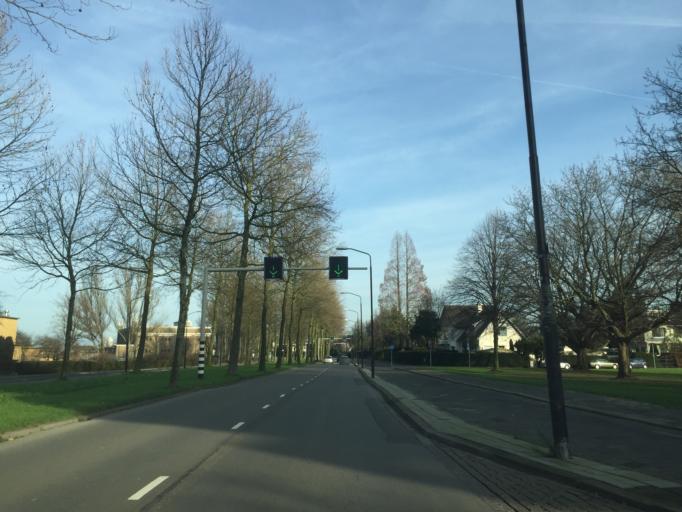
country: NL
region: South Holland
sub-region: Gemeente Dordrecht
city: Dordrecht
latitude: 51.8139
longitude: 4.6853
